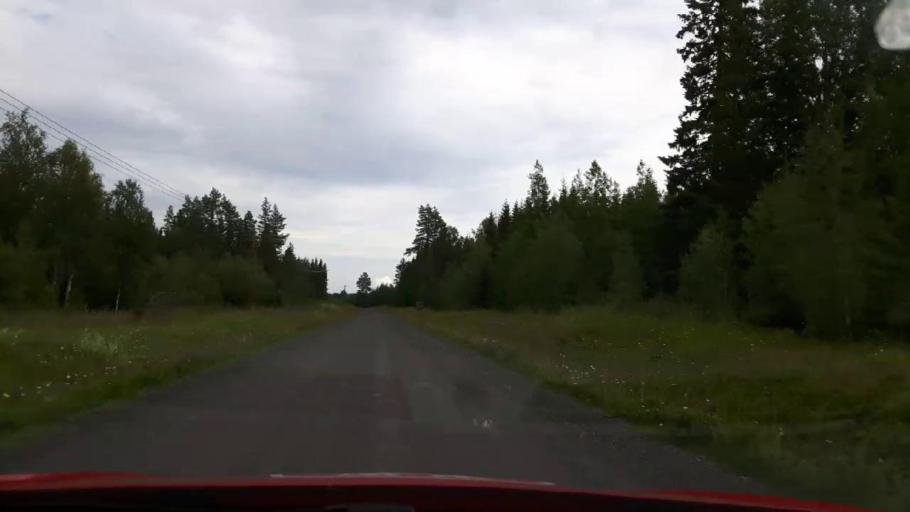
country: SE
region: Jaemtland
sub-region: Stroemsunds Kommun
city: Stroemsund
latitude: 63.4972
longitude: 15.3234
